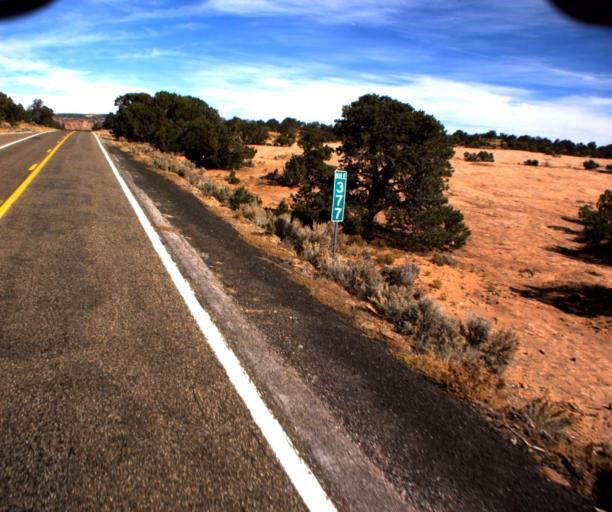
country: US
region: Arizona
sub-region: Navajo County
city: Kayenta
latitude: 36.5958
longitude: -110.4964
